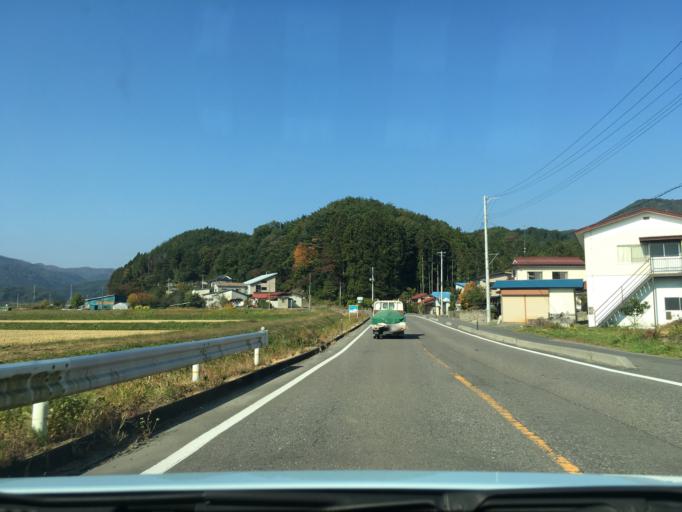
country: JP
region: Fukushima
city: Sukagawa
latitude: 37.2904
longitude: 140.1926
